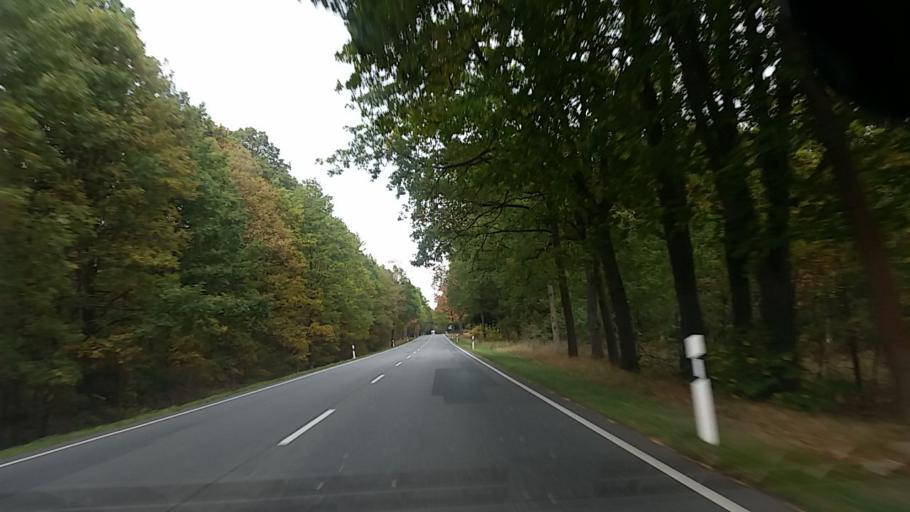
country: DE
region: Lower Saxony
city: Sprakensehl
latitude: 52.8048
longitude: 10.4878
